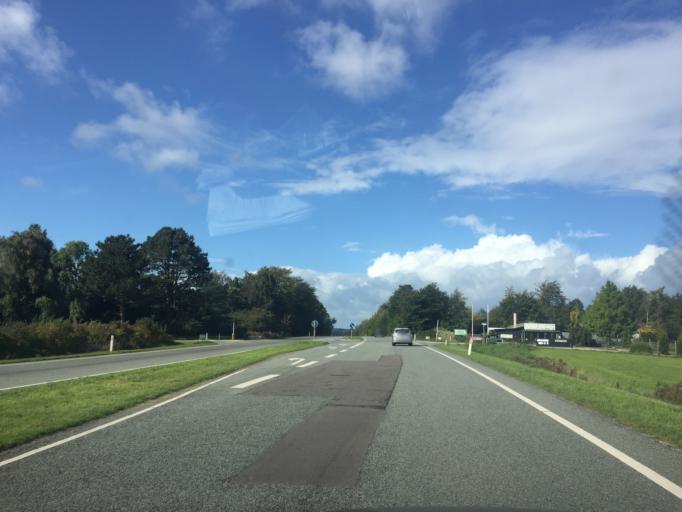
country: DK
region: Capital Region
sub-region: Gribskov Kommune
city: Helsinge
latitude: 56.0360
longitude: 12.1548
